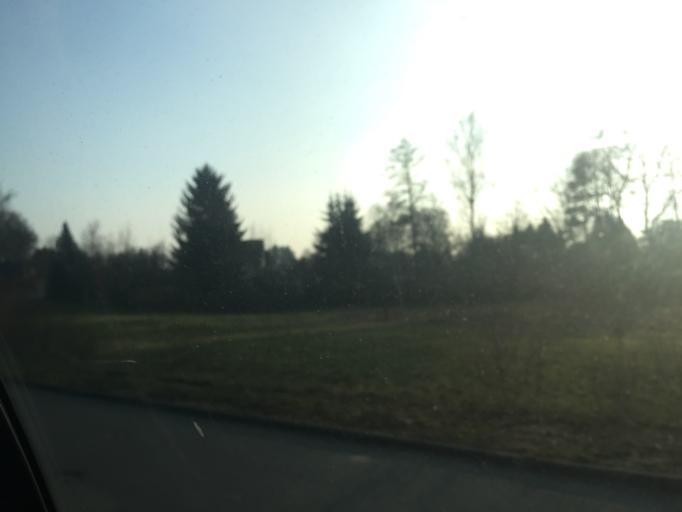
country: DE
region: Saxony
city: Pirna
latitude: 50.9791
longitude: 13.9307
